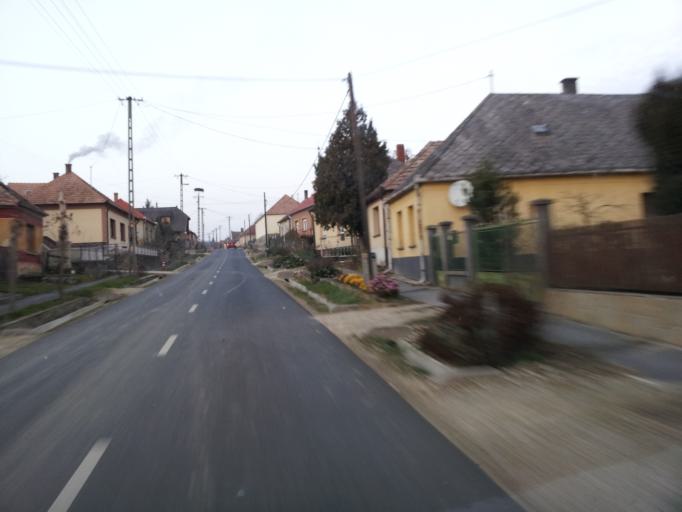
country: HU
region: Zala
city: Zalaszentgrot
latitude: 46.8997
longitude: 17.1536
